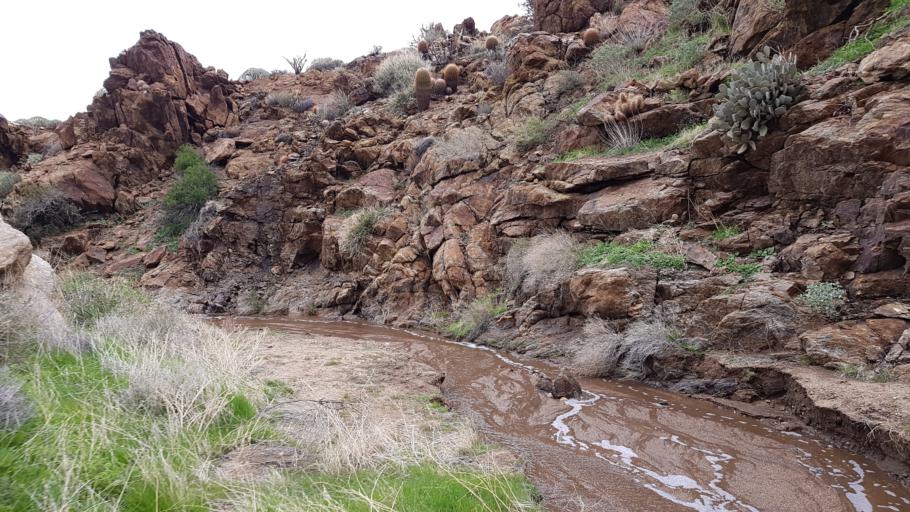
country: US
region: California
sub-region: San Diego County
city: Julian
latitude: 33.1324
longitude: -116.4719
